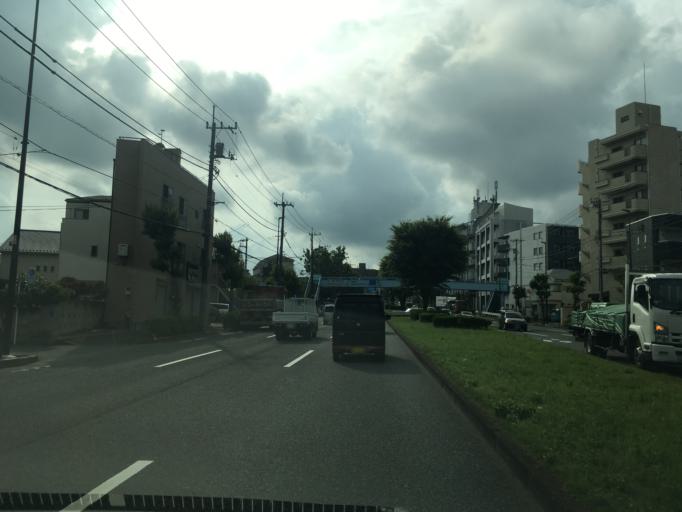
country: JP
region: Tokyo
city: Musashino
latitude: 35.7246
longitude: 139.5585
